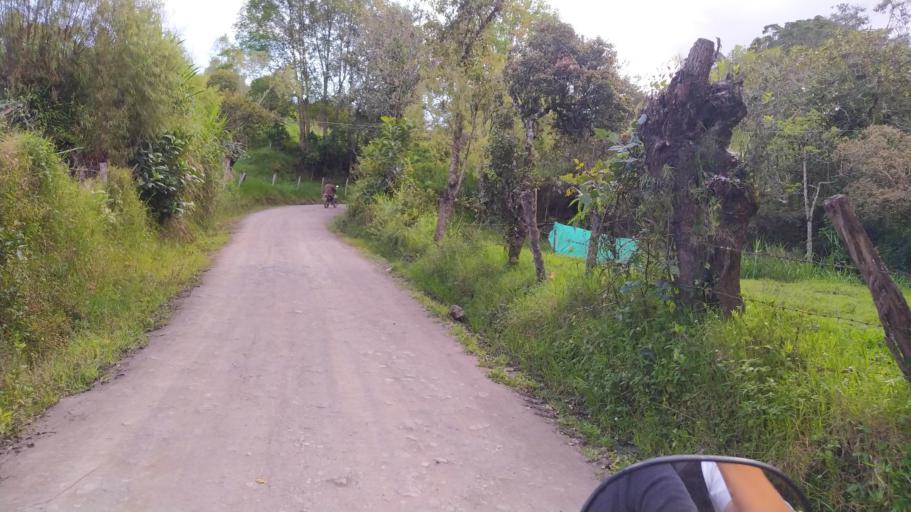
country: CO
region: Cundinamarca
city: Tenza
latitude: 5.0912
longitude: -73.4546
